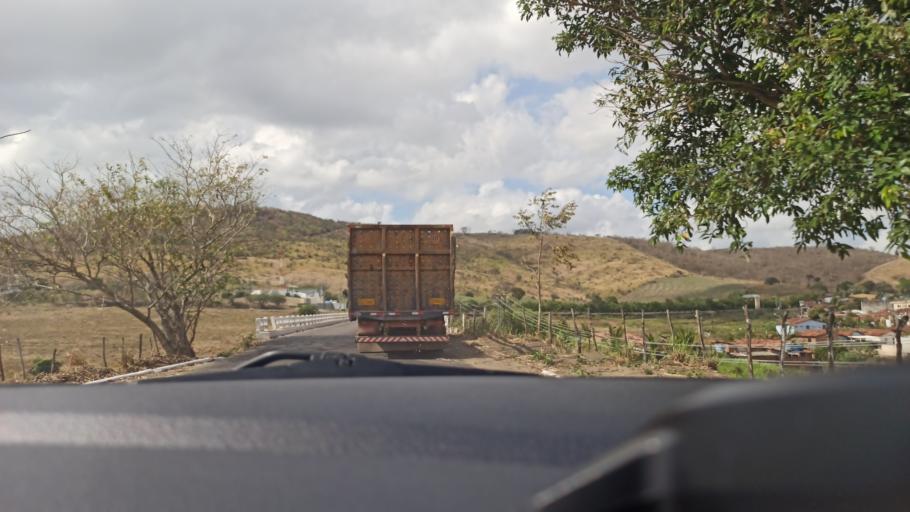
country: BR
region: Pernambuco
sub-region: Timbauba
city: Timbauba
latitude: -7.5179
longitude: -35.3046
